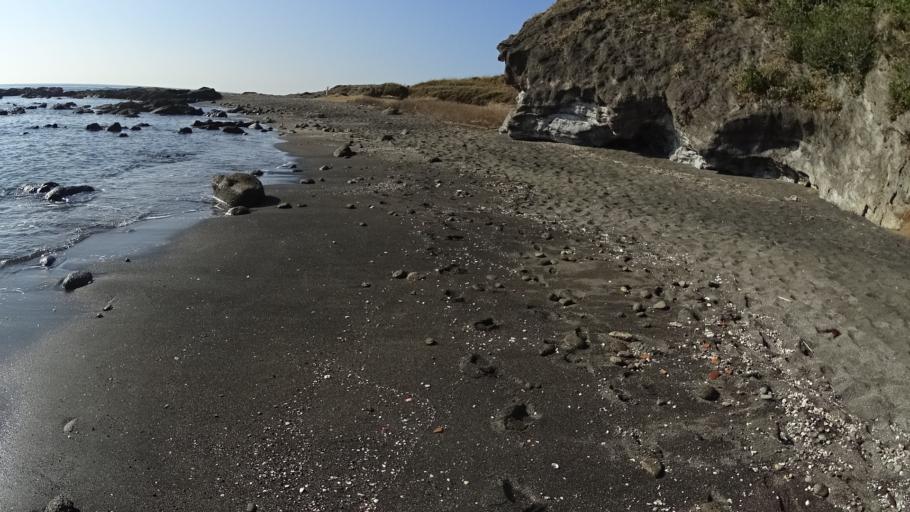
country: JP
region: Kanagawa
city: Miura
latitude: 35.1907
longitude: 139.6114
